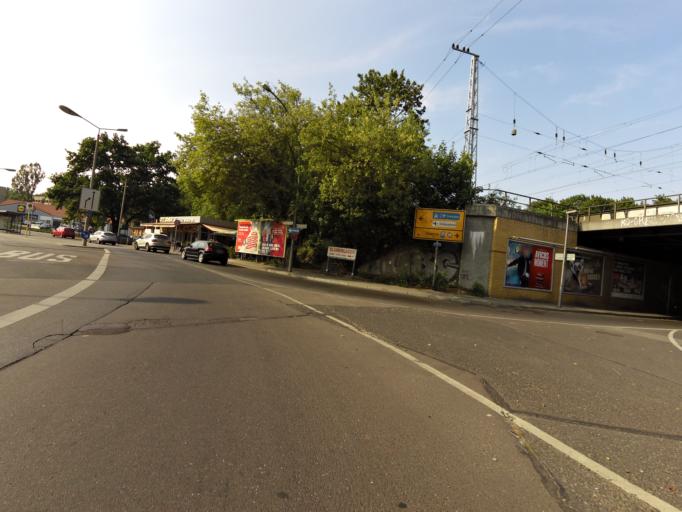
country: DE
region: Berlin
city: Grunau
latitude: 52.4129
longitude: 13.5727
